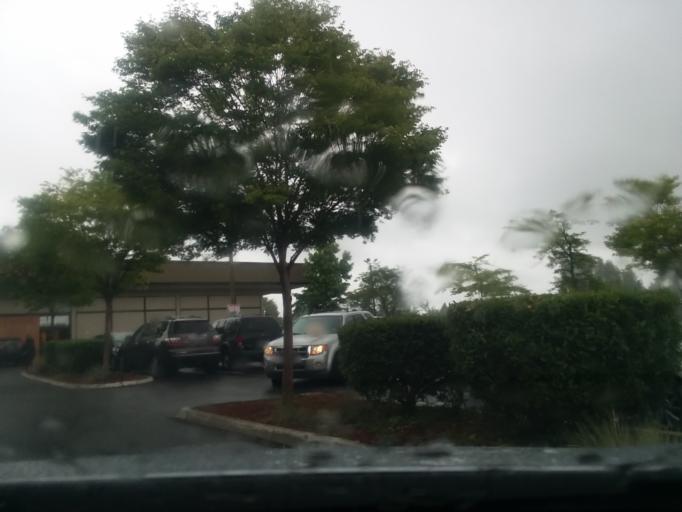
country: US
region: Washington
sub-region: King County
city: Shoreline
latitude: 47.7094
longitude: -122.3193
